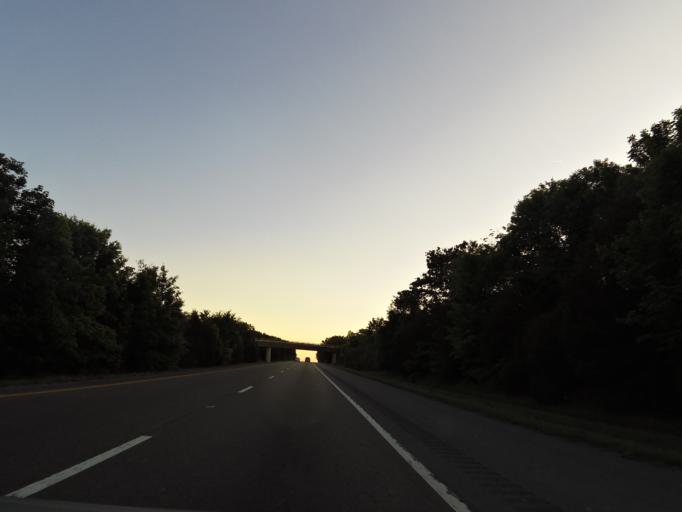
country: US
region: Tennessee
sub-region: Greene County
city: Mosheim
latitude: 36.2511
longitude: -82.9685
